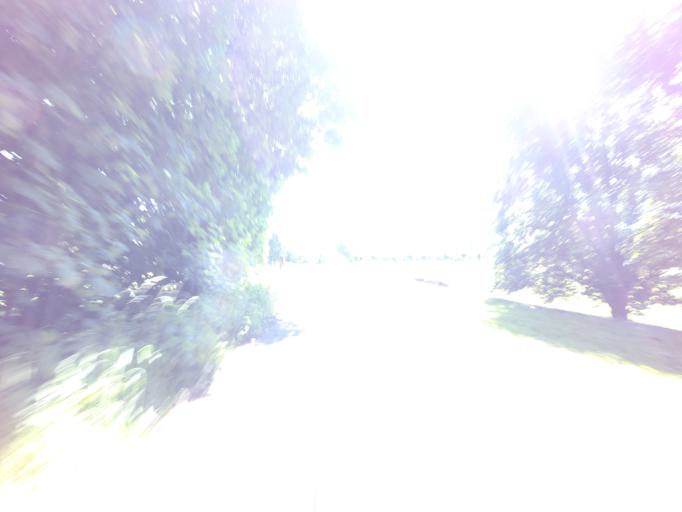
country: DK
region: Central Jutland
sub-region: Horsens Kommune
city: Braedstrup
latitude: 55.9763
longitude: 9.5993
